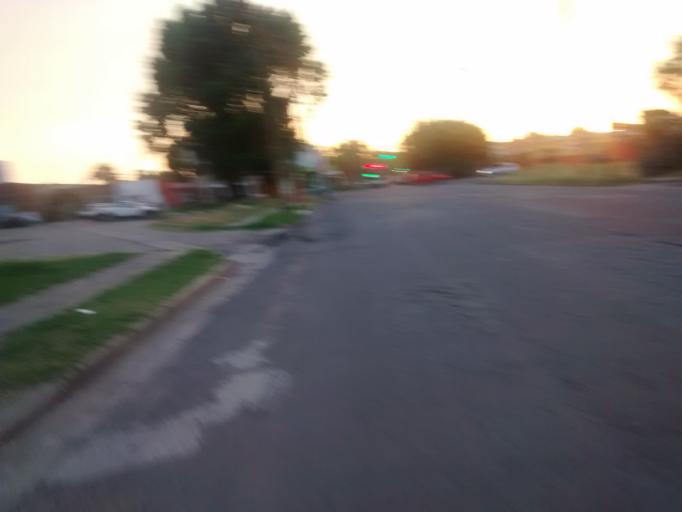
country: AR
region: Buenos Aires
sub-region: Partido de La Plata
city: La Plata
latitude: -34.9420
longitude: -57.9247
